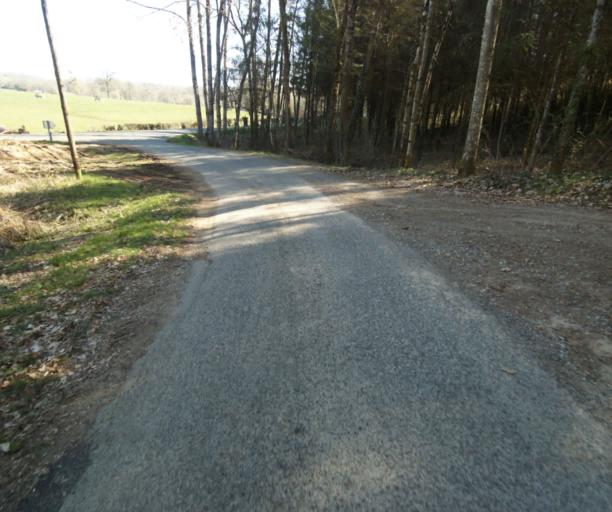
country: FR
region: Limousin
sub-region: Departement de la Correze
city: Saint-Mexant
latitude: 45.3125
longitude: 1.6333
